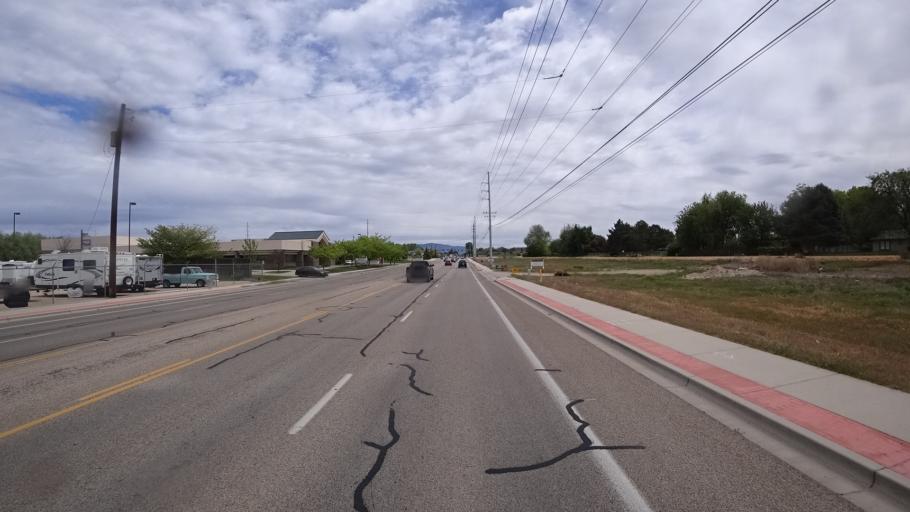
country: US
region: Idaho
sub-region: Ada County
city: Meridian
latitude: 43.5903
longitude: -116.3378
